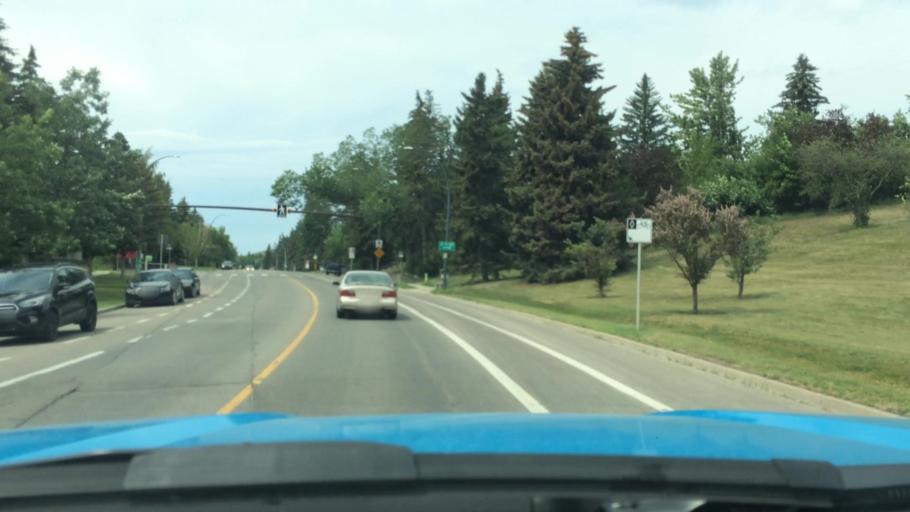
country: CA
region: Alberta
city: Calgary
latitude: 51.0784
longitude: -114.0853
